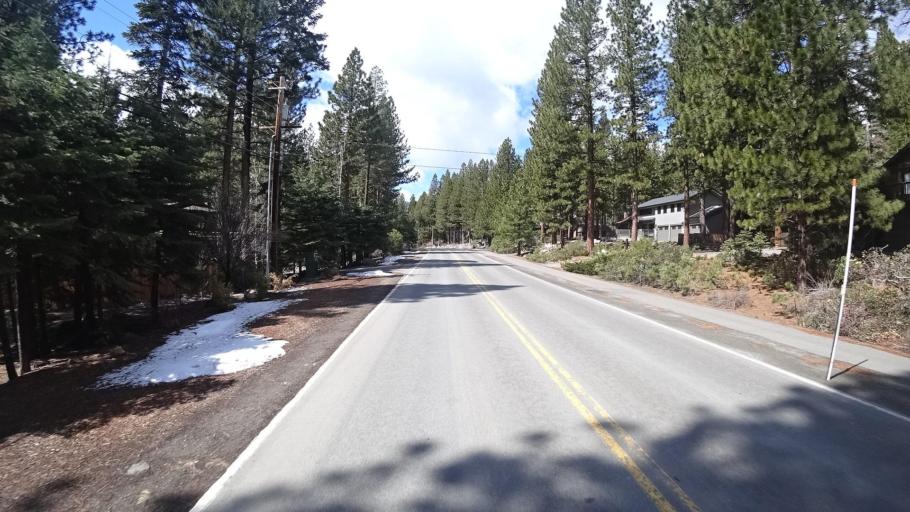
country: US
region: Nevada
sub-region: Washoe County
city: Incline Village
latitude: 39.2476
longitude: -119.9652
